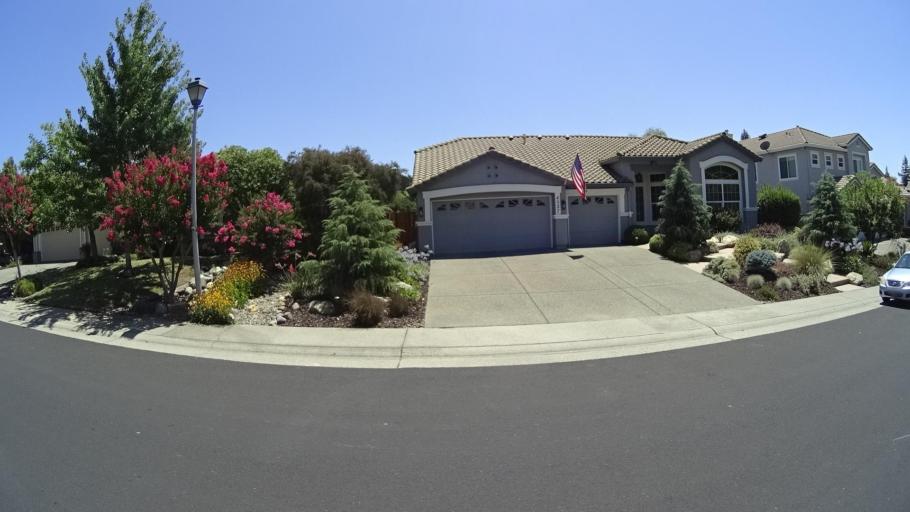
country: US
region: California
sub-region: Placer County
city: Rocklin
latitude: 38.8219
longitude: -121.2490
